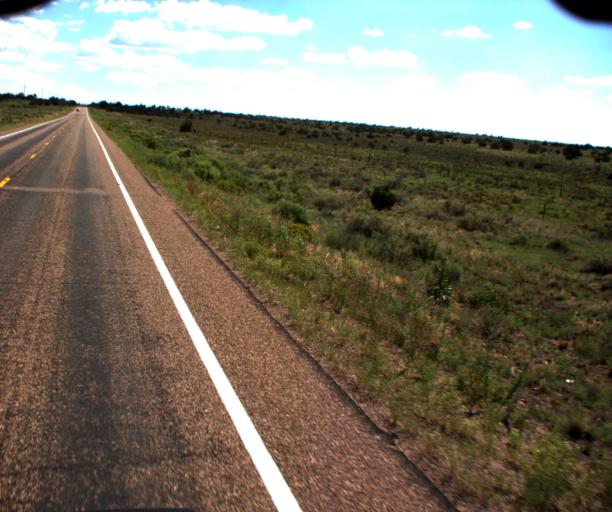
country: US
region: Arizona
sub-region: Coconino County
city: Williams
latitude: 35.5623
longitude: -112.1573
